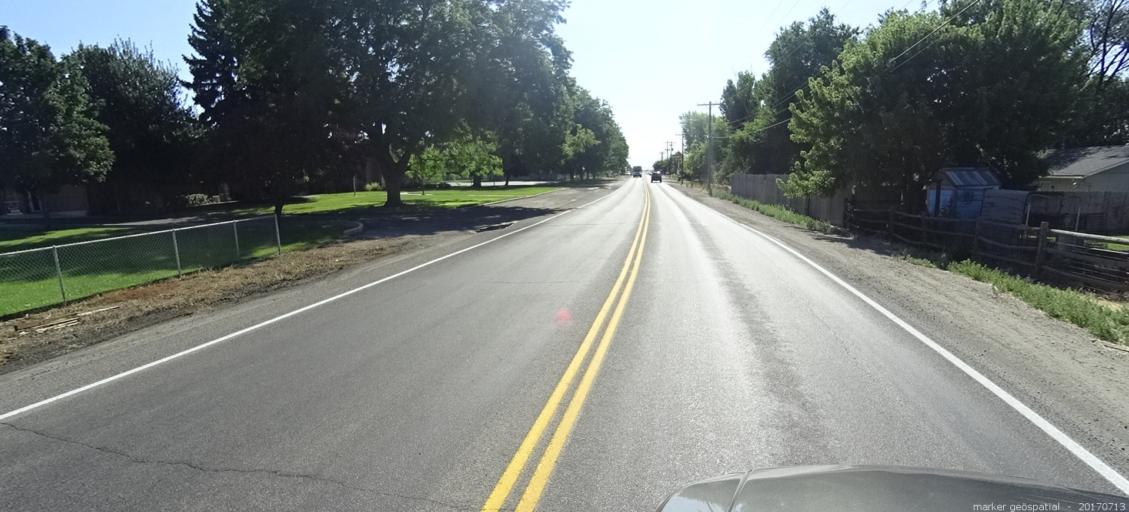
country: US
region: Idaho
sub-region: Ada County
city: Kuna
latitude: 43.4885
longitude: -116.4129
